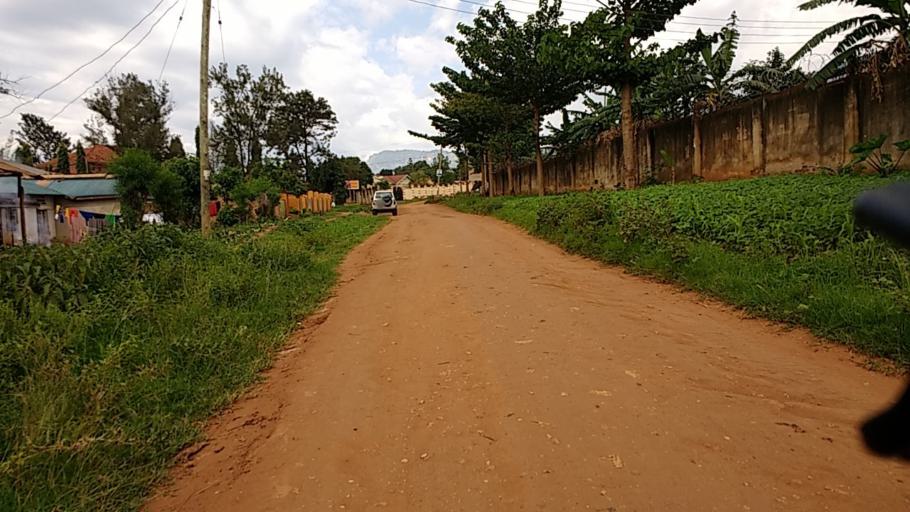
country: UG
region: Eastern Region
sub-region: Mbale District
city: Mbale
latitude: 1.0714
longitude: 34.1685
